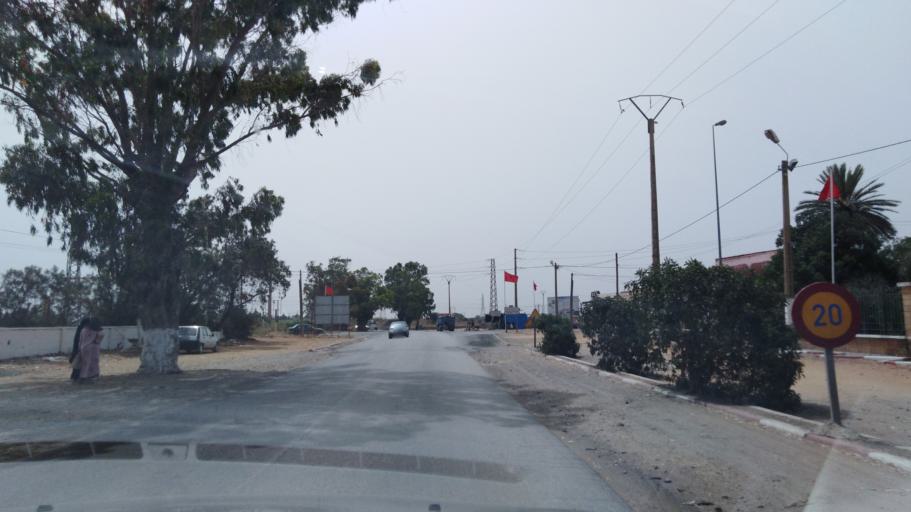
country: MA
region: Grand Casablanca
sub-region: Nouaceur
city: Bouskoura
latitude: 33.3675
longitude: -7.7773
